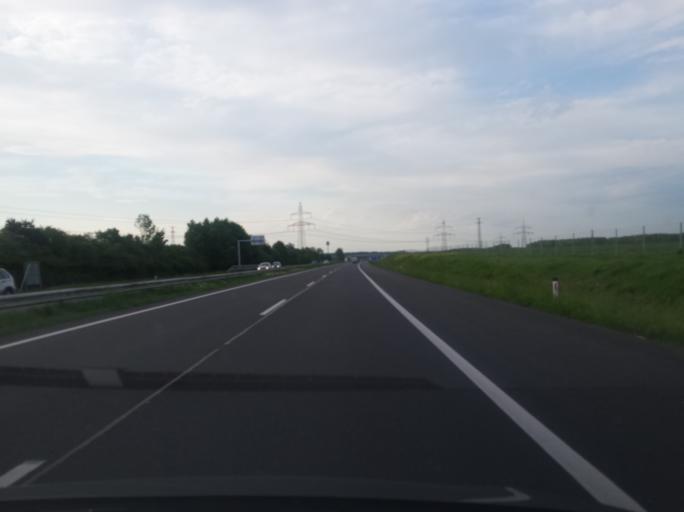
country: AT
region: Burgenland
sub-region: Eisenstadt-Umgebung
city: Hornstein
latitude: 47.8704
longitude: 16.4179
